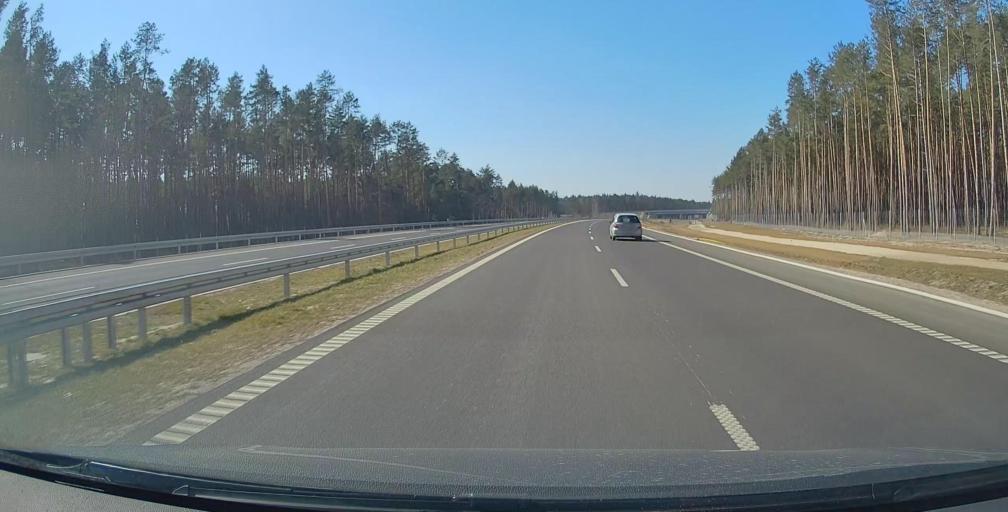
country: PL
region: Subcarpathian Voivodeship
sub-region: Powiat nizanski
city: Jarocin
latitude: 50.6011
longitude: 22.2832
